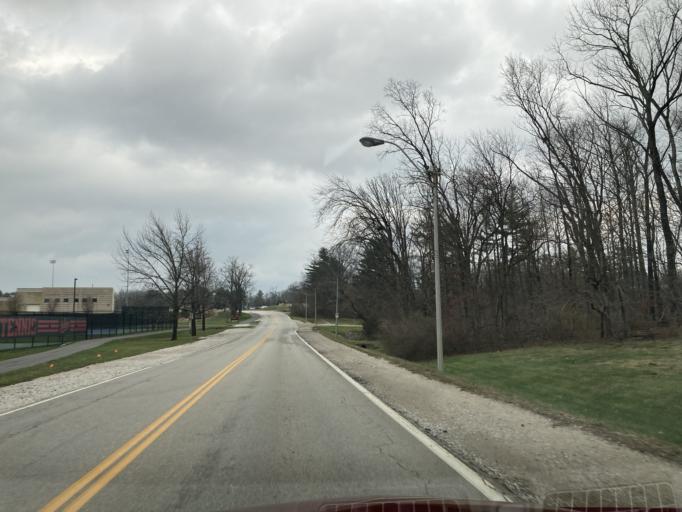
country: US
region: Indiana
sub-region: Monroe County
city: Bloomington
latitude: 39.1827
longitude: -86.5192
